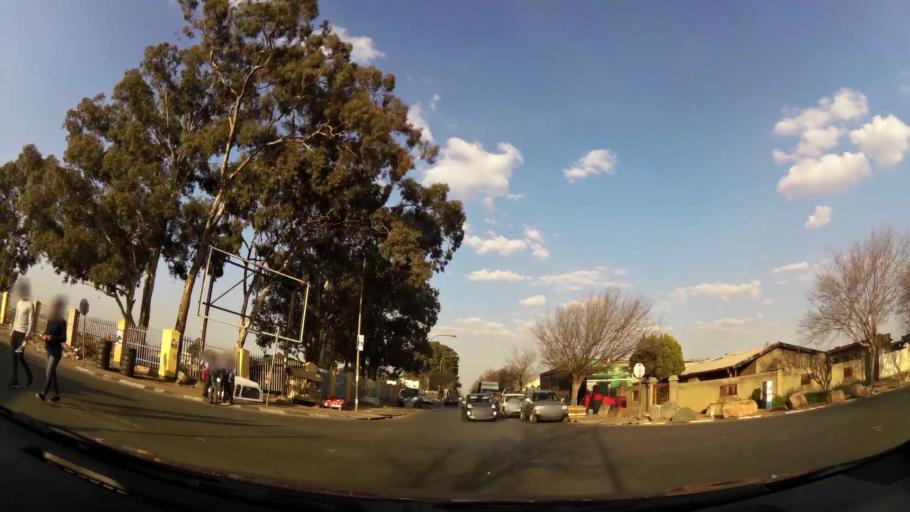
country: ZA
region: Gauteng
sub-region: City of Johannesburg Metropolitan Municipality
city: Roodepoort
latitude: -26.2158
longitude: 27.8935
